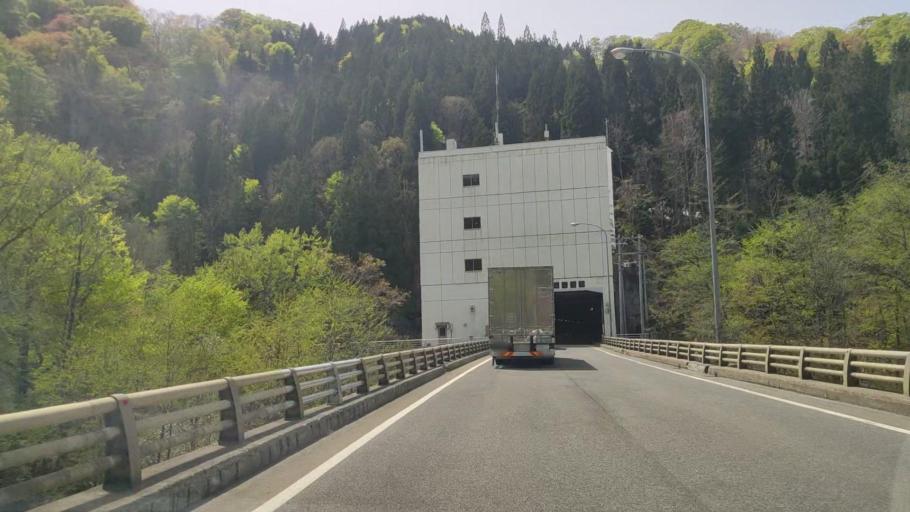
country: JP
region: Aomori
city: Aomori Shi
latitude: 40.7732
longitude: 140.9872
